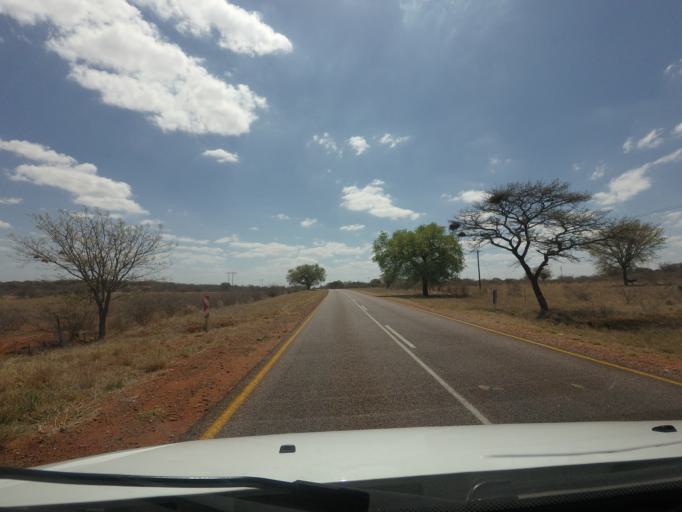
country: ZA
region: Limpopo
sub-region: Capricorn District Municipality
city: Dendron
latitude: -23.5572
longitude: 28.7492
